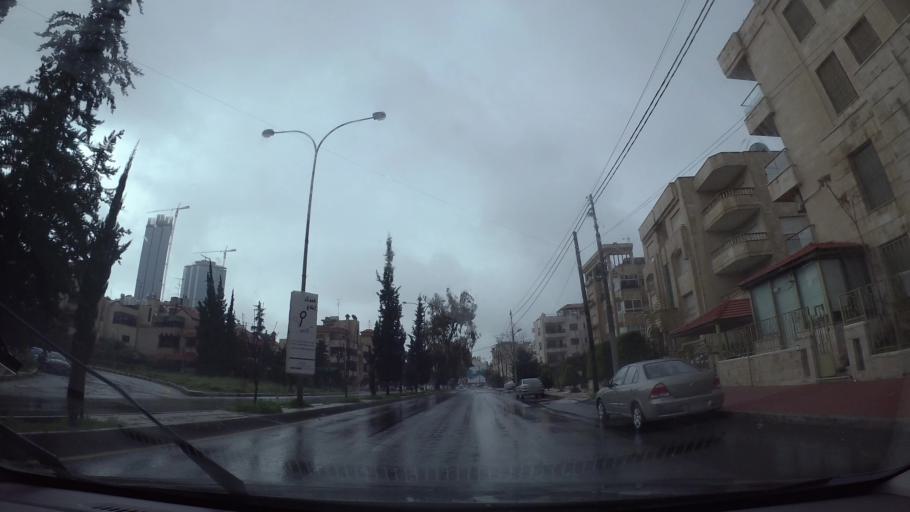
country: JO
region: Amman
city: Wadi as Sir
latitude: 31.9663
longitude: 35.8643
